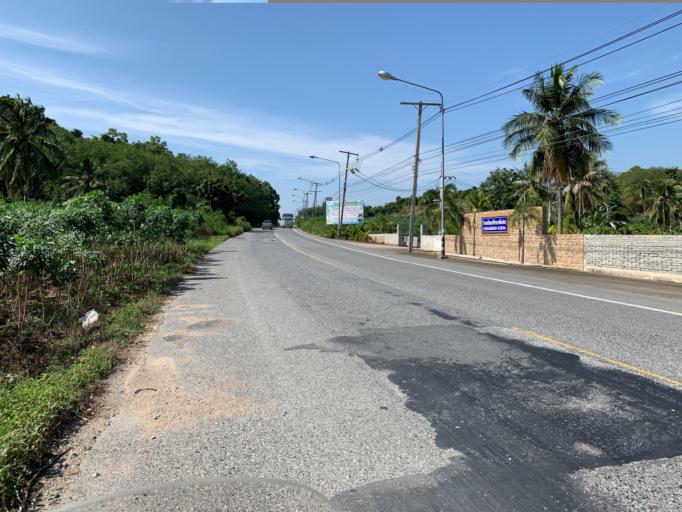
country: TH
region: Rayong
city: Ban Chang
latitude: 12.8185
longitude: 100.9920
